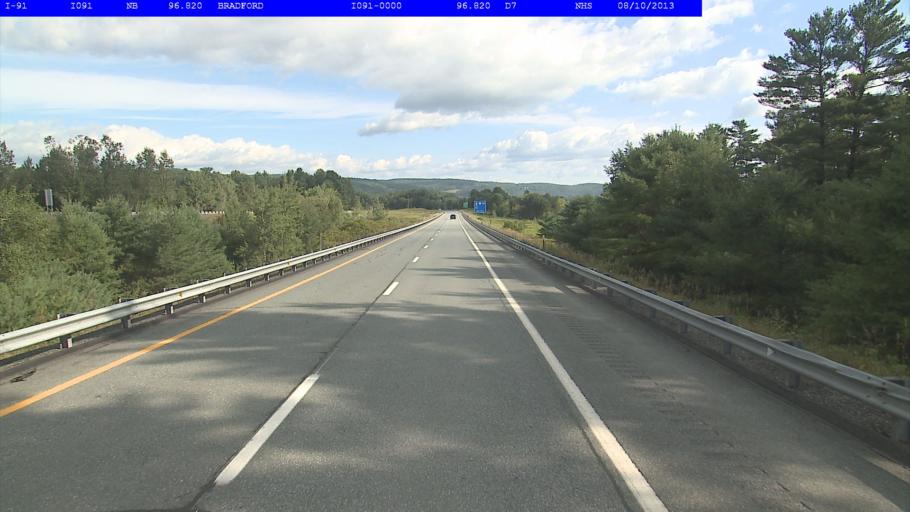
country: US
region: New Hampshire
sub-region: Grafton County
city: Orford
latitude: 43.9733
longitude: -72.1255
